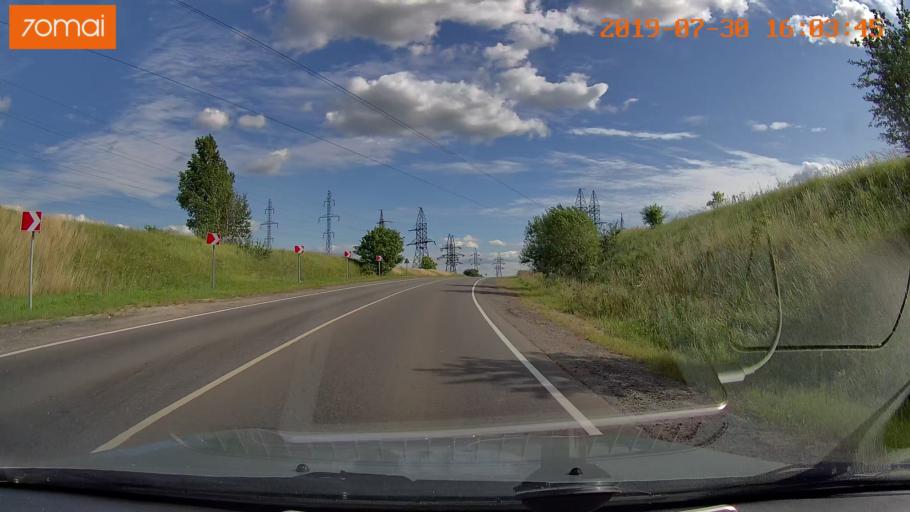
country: RU
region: Moskovskaya
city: Voskresensk
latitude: 55.2878
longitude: 38.6993
